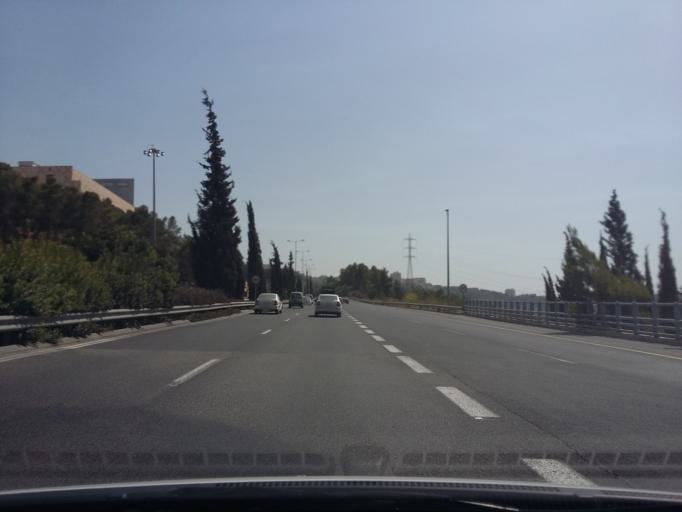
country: IL
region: Jerusalem
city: West Jerusalem
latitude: 31.8074
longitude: 35.2075
